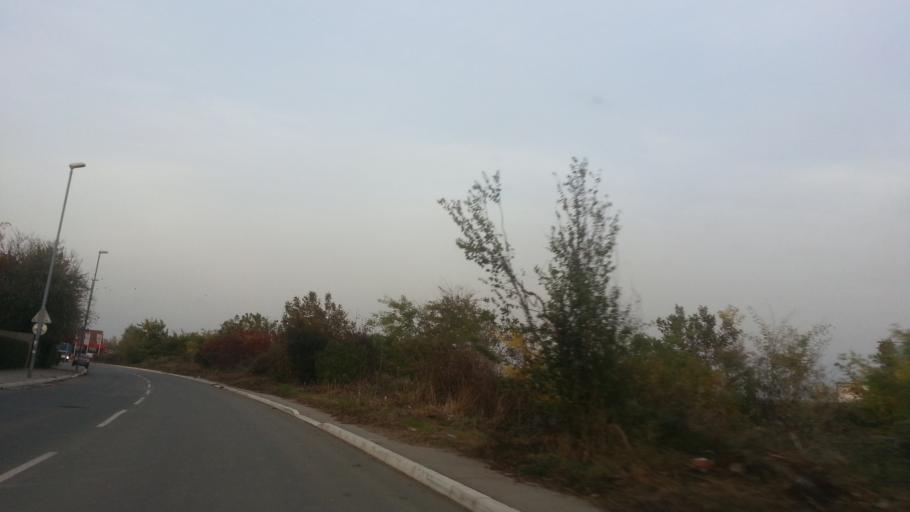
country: RS
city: Novi Banovci
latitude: 44.8919
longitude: 20.2936
